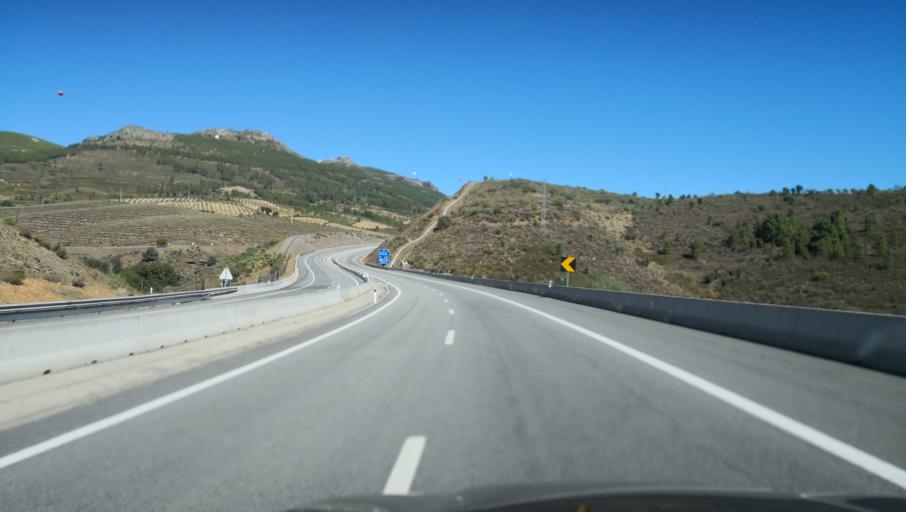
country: PT
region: Vila Real
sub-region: Murca
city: Murca
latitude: 41.4246
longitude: -7.3615
